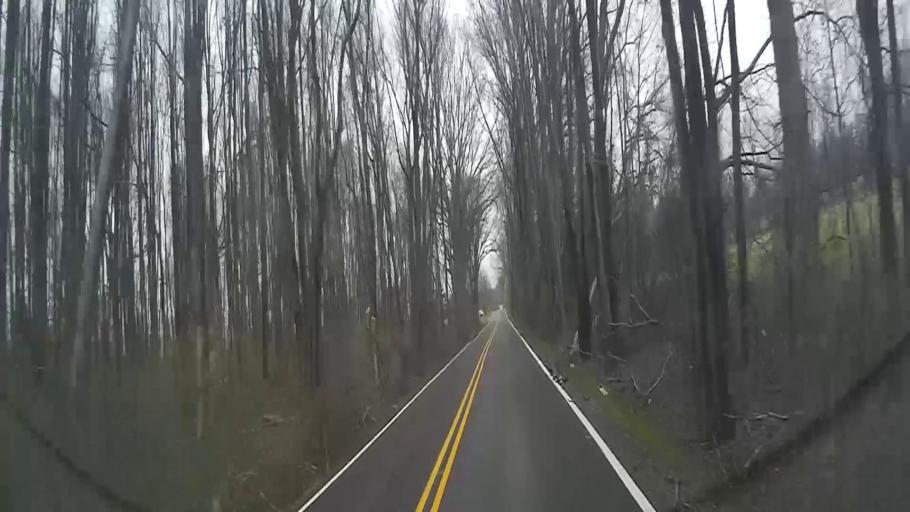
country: US
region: New Jersey
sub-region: Burlington County
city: Marlton
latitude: 39.8788
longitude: -74.8858
